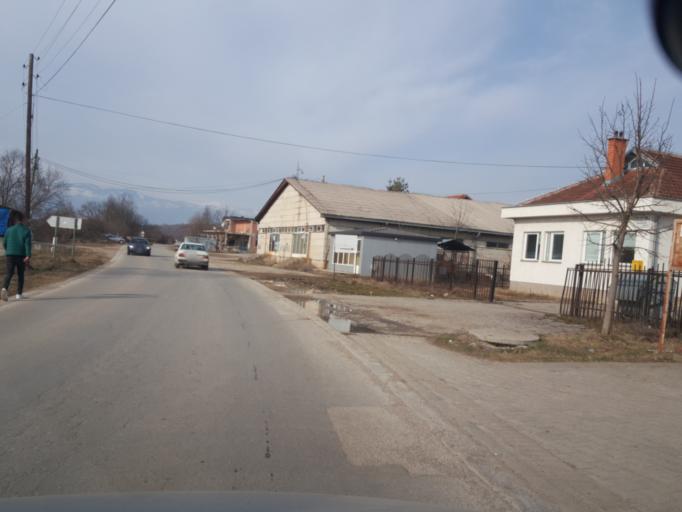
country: XK
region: Pec
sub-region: Komuna e Klines
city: Klina
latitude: 42.6632
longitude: 20.5393
